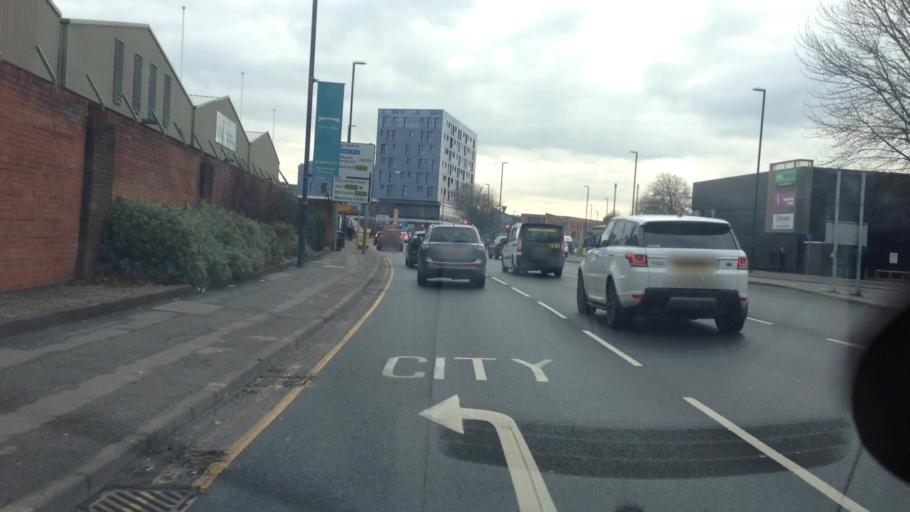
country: GB
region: England
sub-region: City and Borough of Leeds
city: Leeds
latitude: 53.7910
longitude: -1.5427
